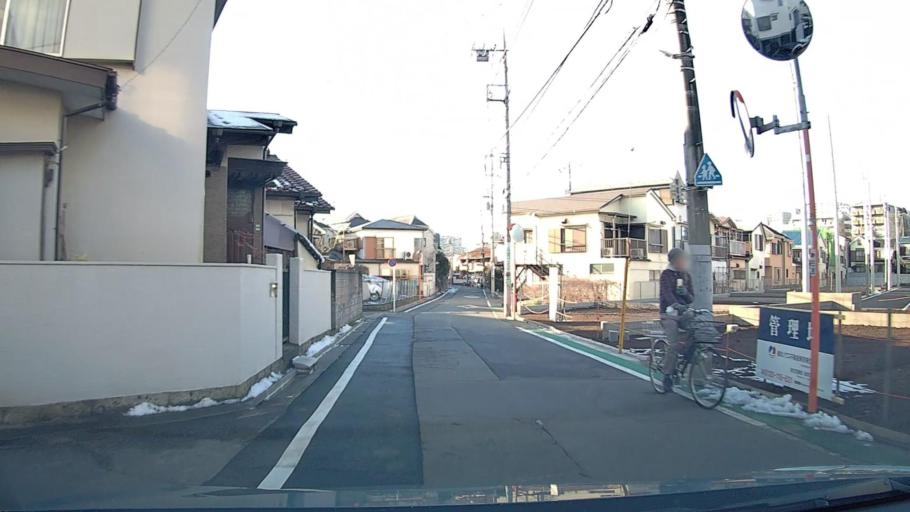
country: JP
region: Saitama
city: Wako
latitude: 35.7519
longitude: 139.6329
